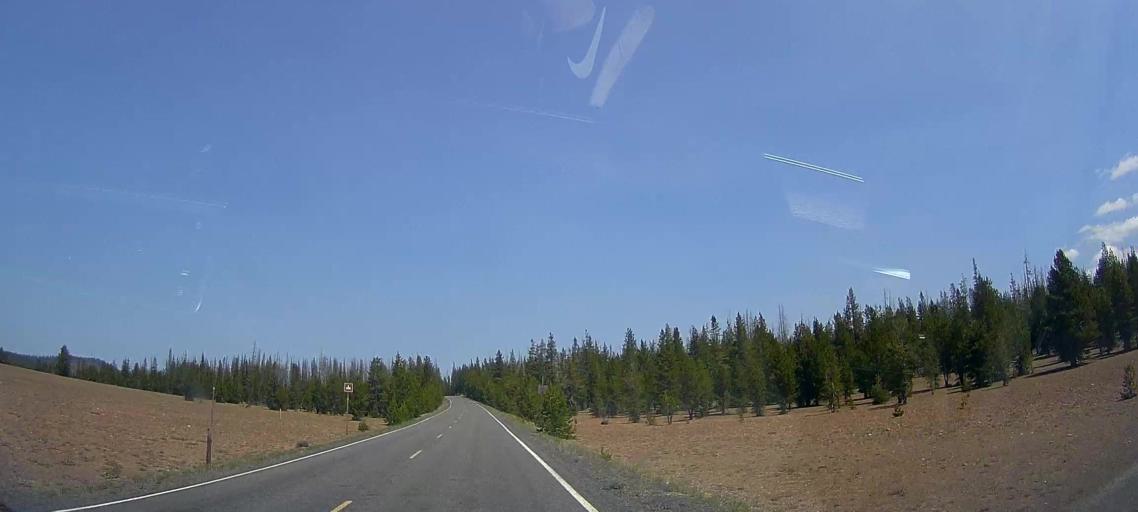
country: US
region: Oregon
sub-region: Lane County
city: Oakridge
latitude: 43.0347
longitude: -122.1173
